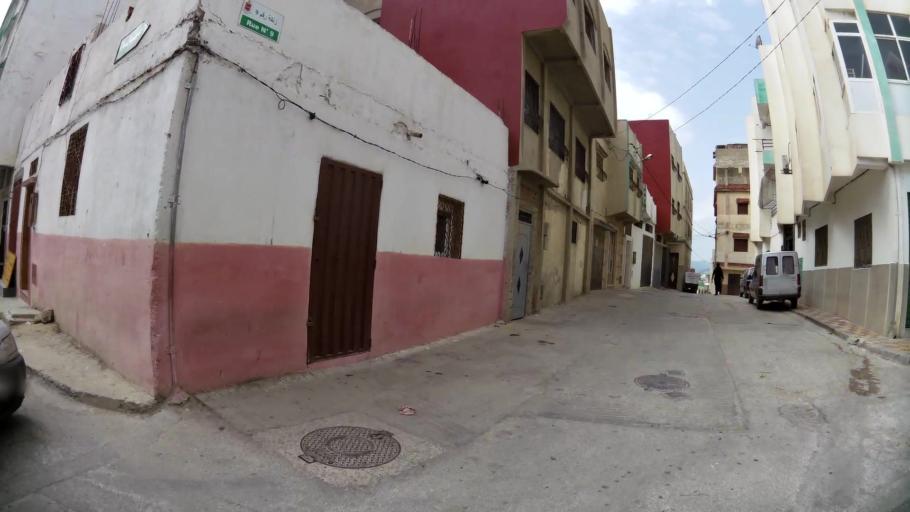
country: MA
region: Tanger-Tetouan
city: Tetouan
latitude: 35.5716
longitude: -5.3963
